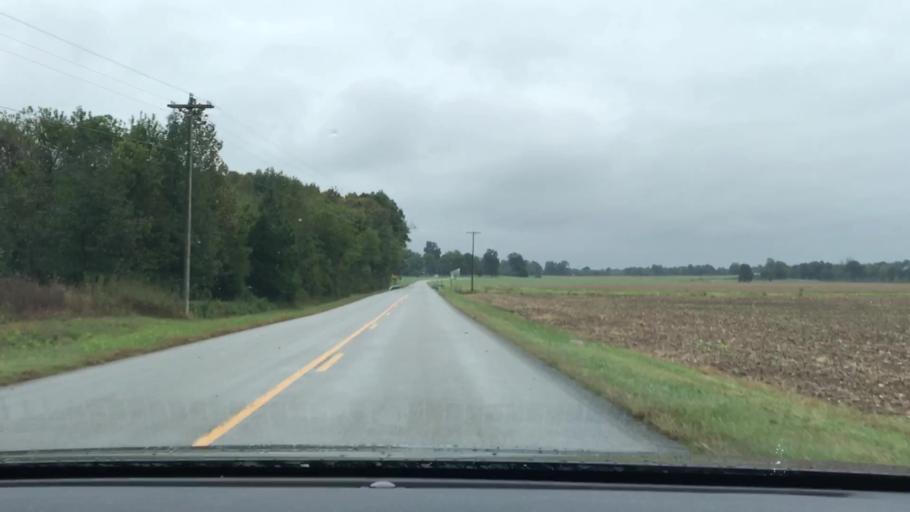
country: US
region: Kentucky
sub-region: McLean County
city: Calhoun
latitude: 37.4728
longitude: -87.2393
